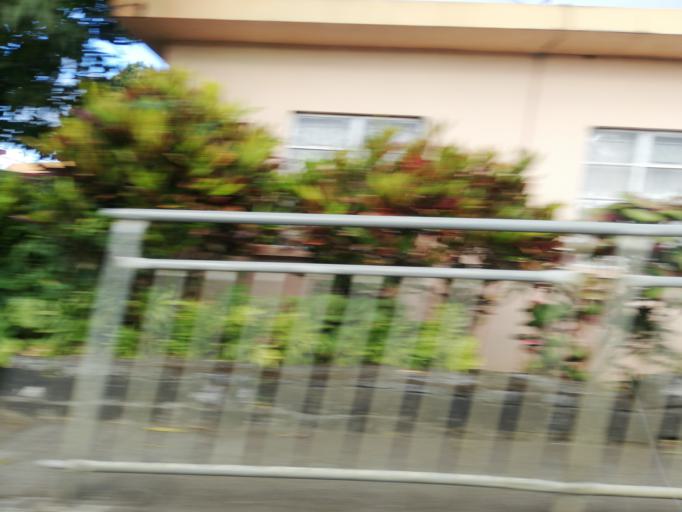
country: MU
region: Flacq
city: Camp de Masque
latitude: -20.2326
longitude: 57.6772
